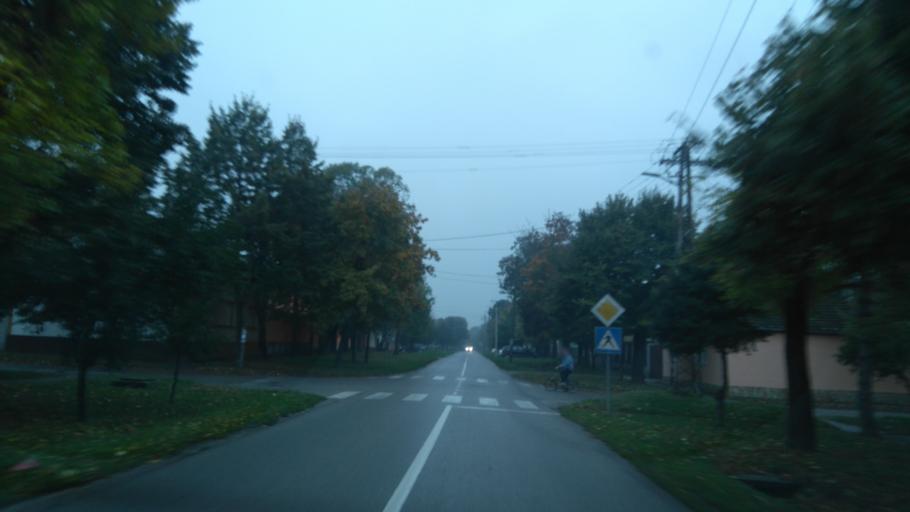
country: RS
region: Autonomna Pokrajina Vojvodina
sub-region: Juznobacki Okrug
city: Becej
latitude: 45.6100
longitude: 20.0452
